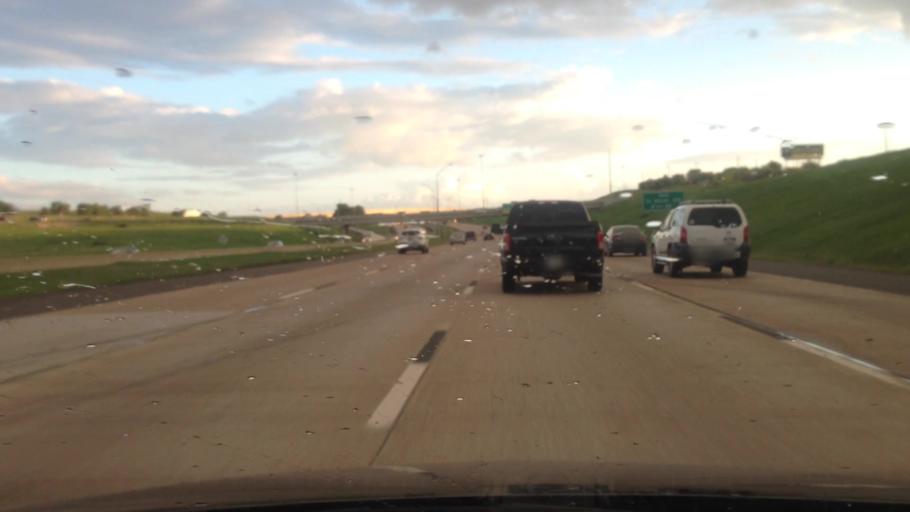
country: US
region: Texas
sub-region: Tarrant County
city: White Settlement
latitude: 32.7468
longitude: -97.4807
